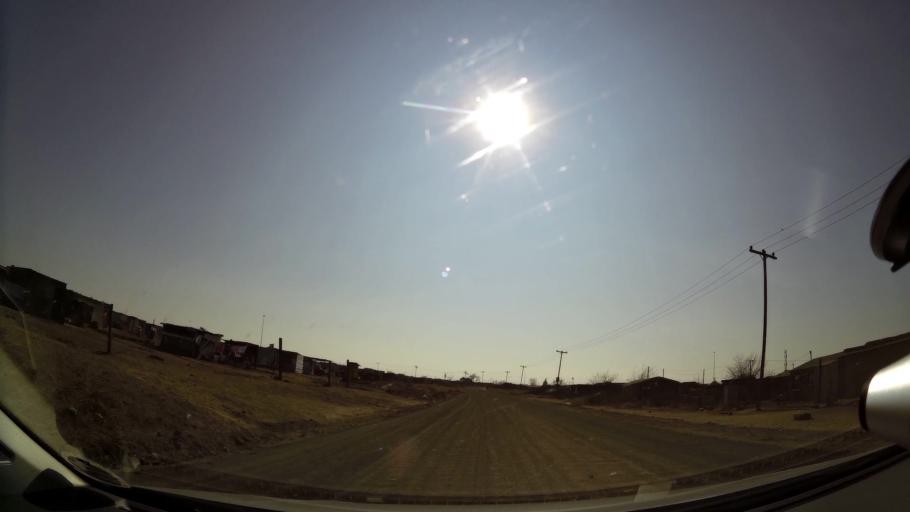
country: ZA
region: Orange Free State
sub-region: Mangaung Metropolitan Municipality
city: Bloemfontein
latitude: -29.1880
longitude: 26.2845
